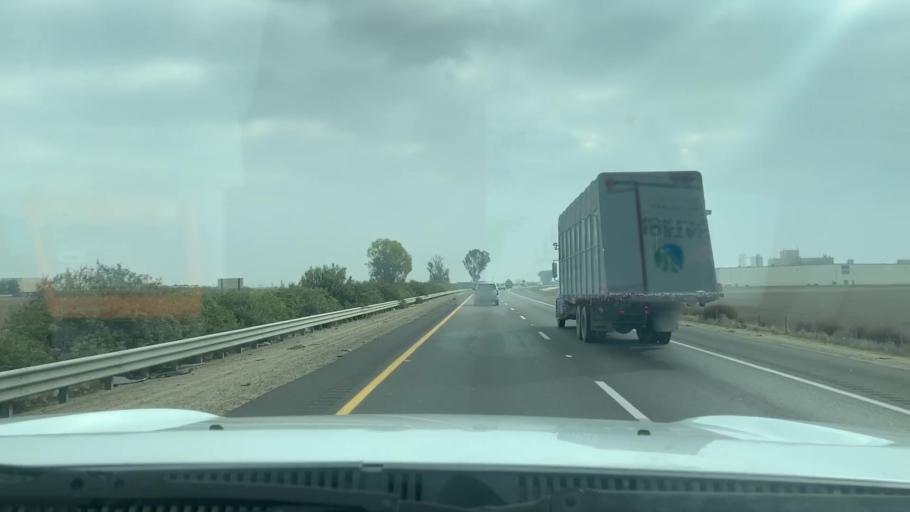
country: US
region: California
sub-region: Tulare County
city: Tulare
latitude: 36.1366
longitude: -119.3268
